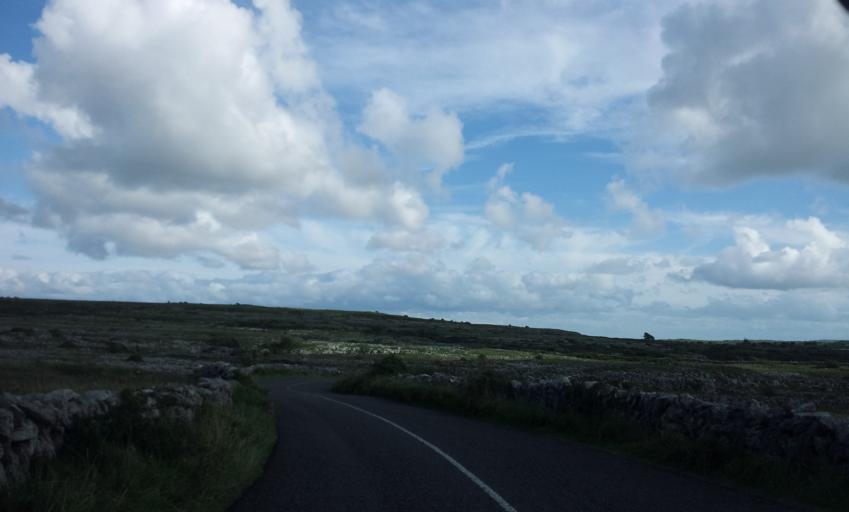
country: IE
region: Connaught
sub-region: County Galway
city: Bearna
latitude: 53.0584
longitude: -9.1465
